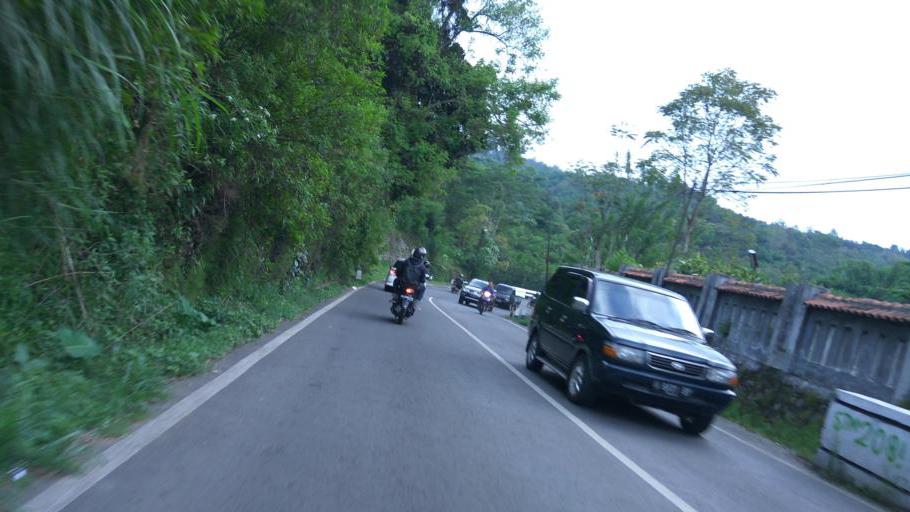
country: ID
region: Central Java
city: Gunung Kendil
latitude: -7.3758
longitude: 110.4351
